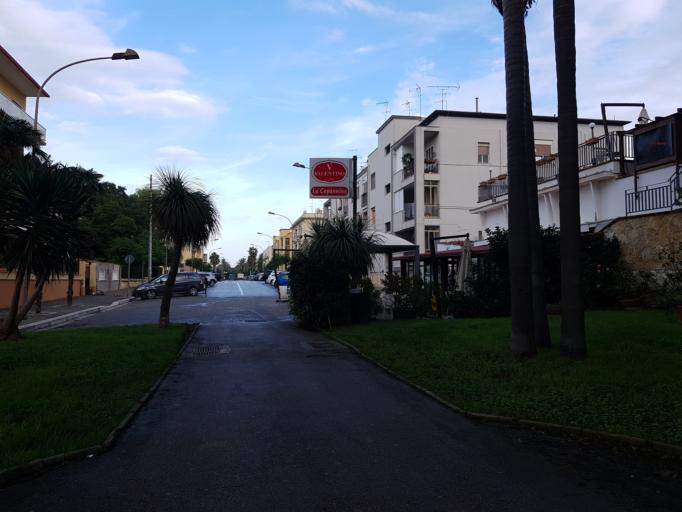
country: IT
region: Apulia
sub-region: Provincia di Brindisi
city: Materdomini
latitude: 40.6451
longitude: 17.9467
